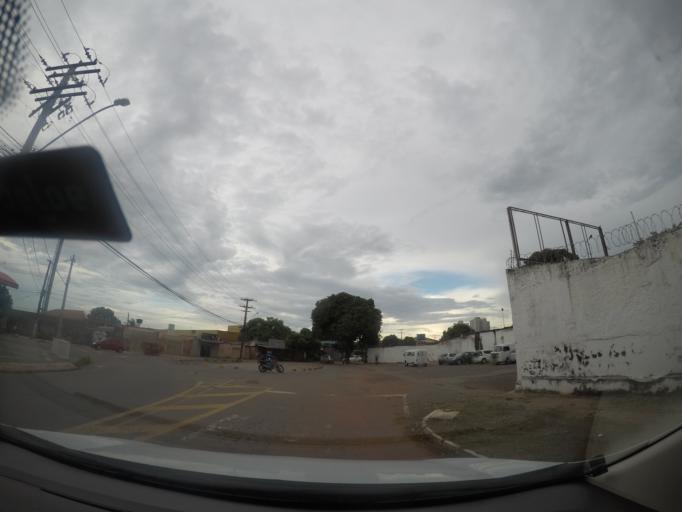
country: BR
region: Goias
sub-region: Goiania
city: Goiania
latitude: -16.6563
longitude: -49.2509
